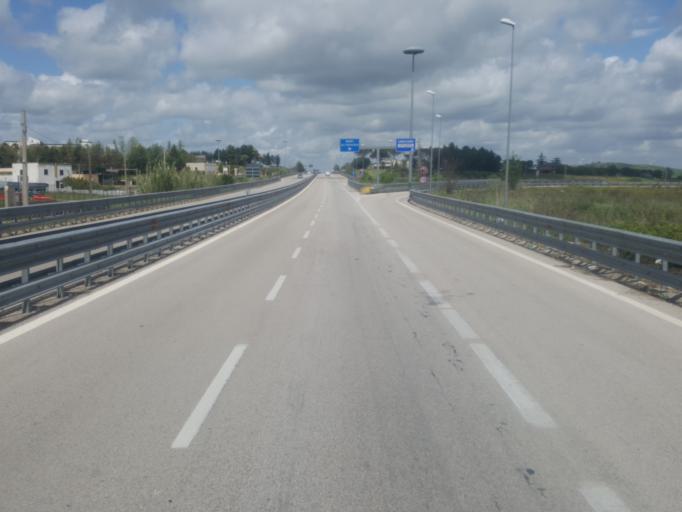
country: IT
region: Basilicate
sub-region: Provincia di Matera
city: Matera
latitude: 40.6971
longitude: 16.5902
